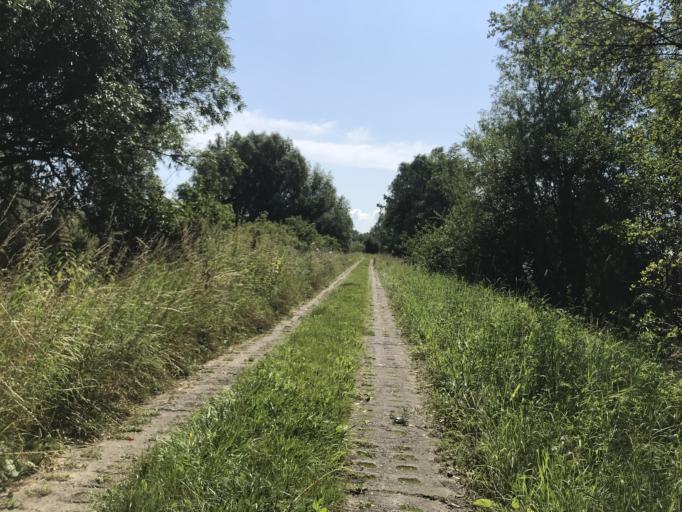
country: PL
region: Pomeranian Voivodeship
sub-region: Gdansk
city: Gdansk
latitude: 54.3243
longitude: 18.6643
